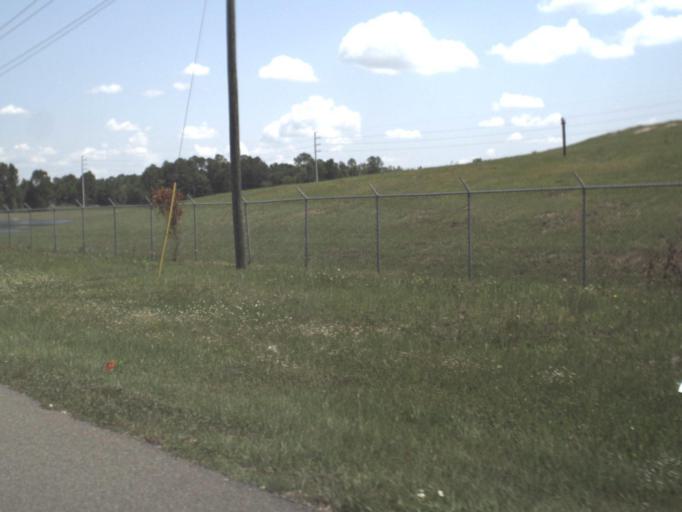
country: US
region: Florida
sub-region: Clay County
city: Keystone Heights
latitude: 29.8095
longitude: -82.0654
